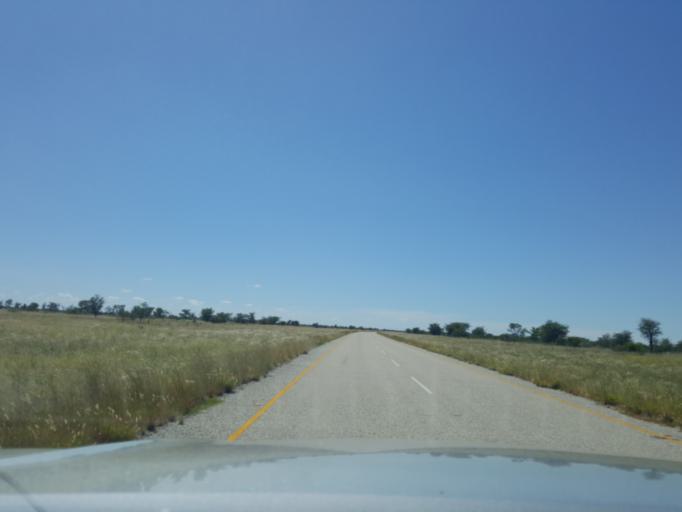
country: BW
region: Central
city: Gweta
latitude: -20.2223
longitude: 25.0204
